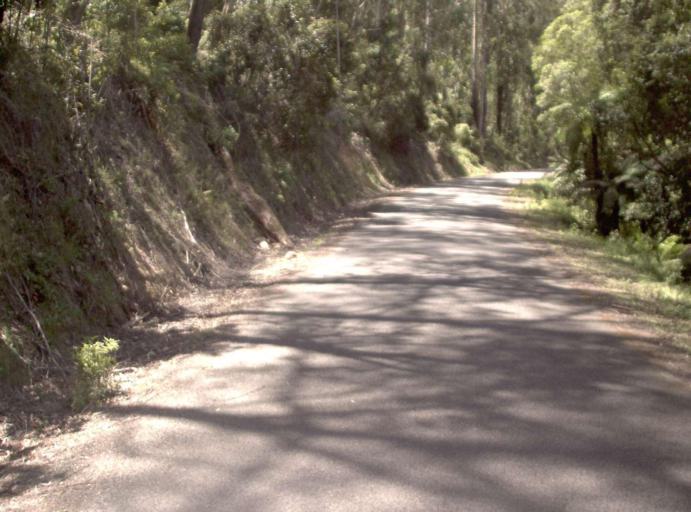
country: AU
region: New South Wales
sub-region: Bombala
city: Bombala
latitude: -37.4538
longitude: 148.9308
